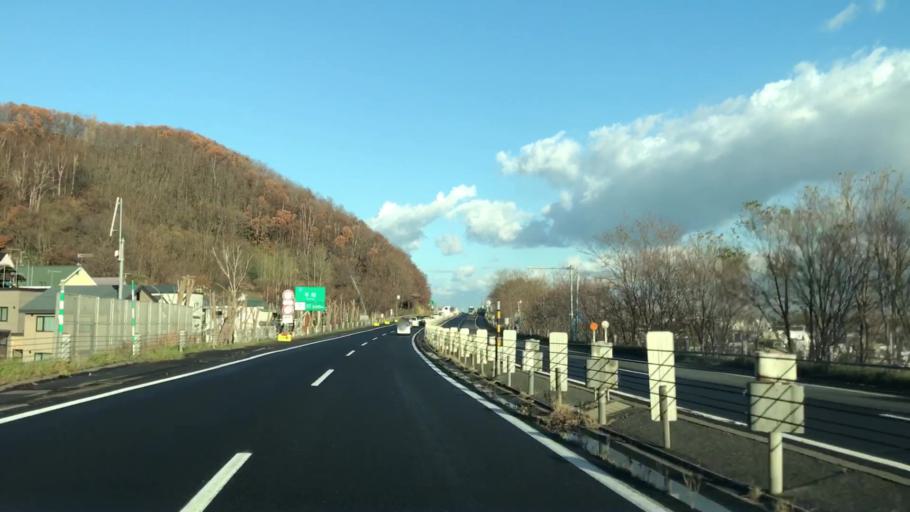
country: JP
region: Hokkaido
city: Sapporo
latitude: 43.1049
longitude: 141.2433
